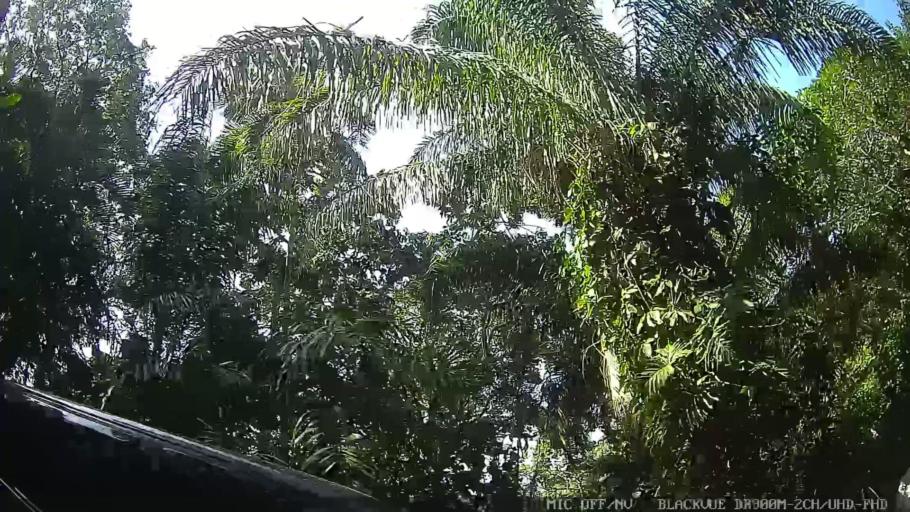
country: BR
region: Sao Paulo
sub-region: Guaruja
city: Guaruja
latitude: -23.9866
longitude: -46.1869
